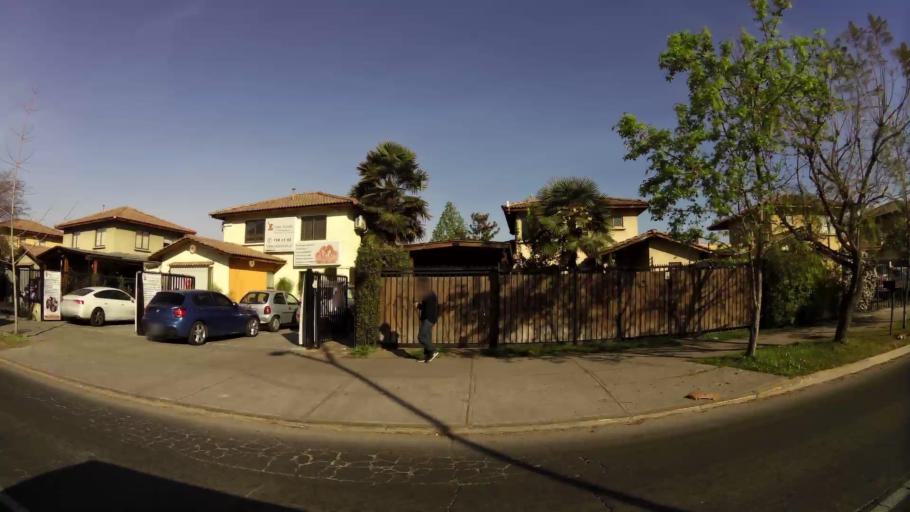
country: CL
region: Santiago Metropolitan
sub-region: Provincia de Santiago
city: Villa Presidente Frei, Nunoa, Santiago, Chile
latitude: -33.4863
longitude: -70.5488
